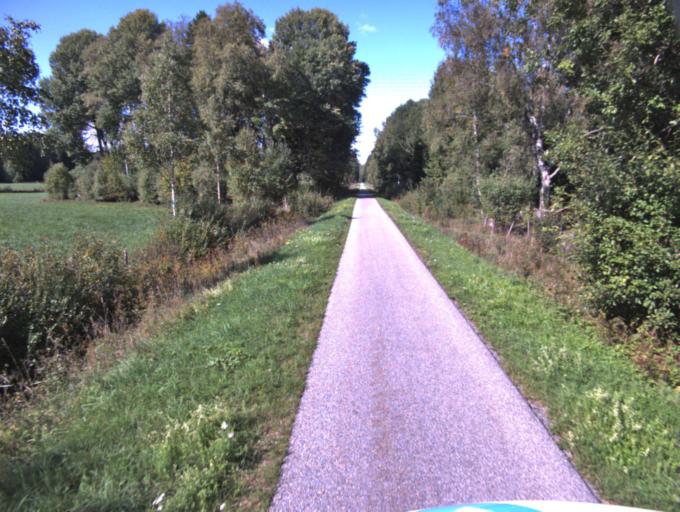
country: SE
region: Vaestra Goetaland
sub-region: Ulricehamns Kommun
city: Ulricehamn
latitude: 57.8321
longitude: 13.3417
